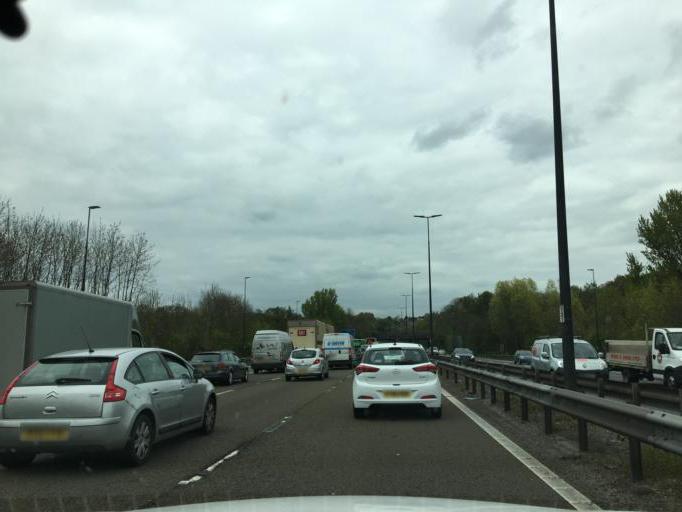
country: GB
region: Wales
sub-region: Newport
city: Newport
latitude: 51.5727
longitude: -3.0331
